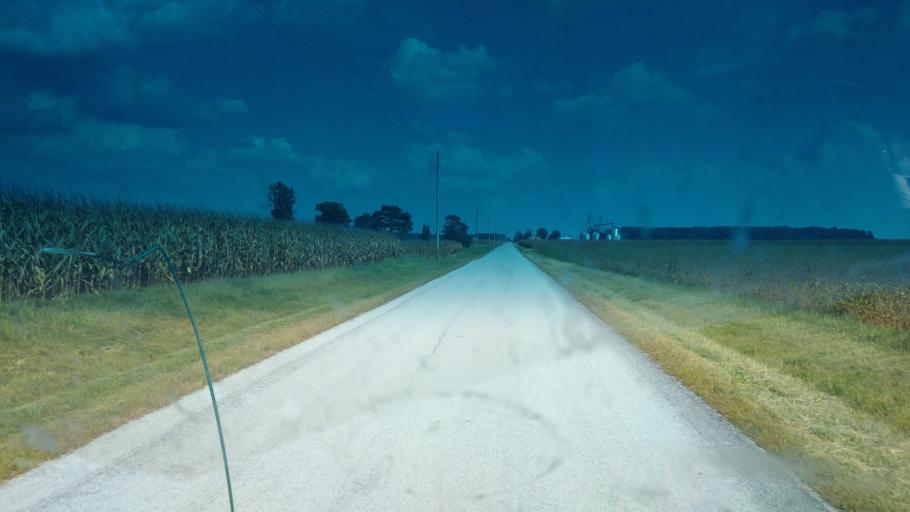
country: US
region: Ohio
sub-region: Hardin County
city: Kenton
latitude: 40.6590
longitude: -83.7205
